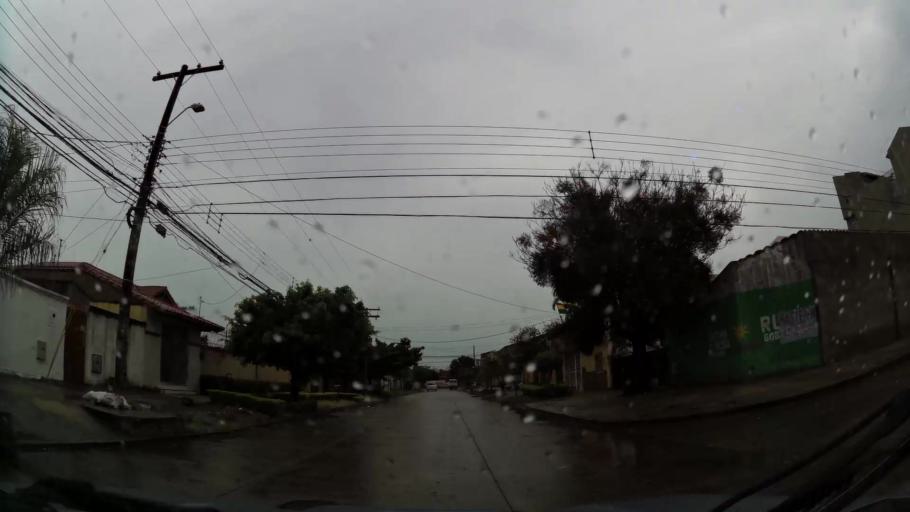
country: BO
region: Santa Cruz
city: Santa Cruz de la Sierra
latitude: -17.7733
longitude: -63.1530
